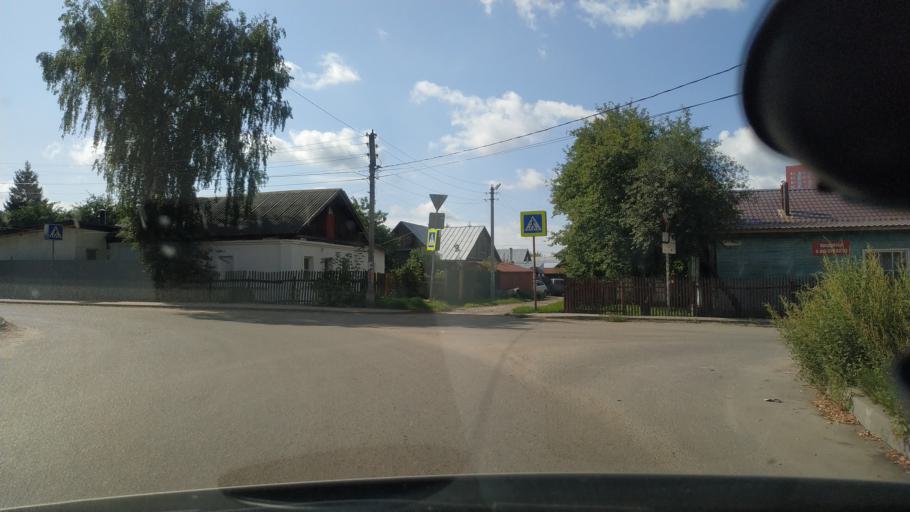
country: RU
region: Rjazan
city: Ryazan'
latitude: 54.6172
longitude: 39.7075
